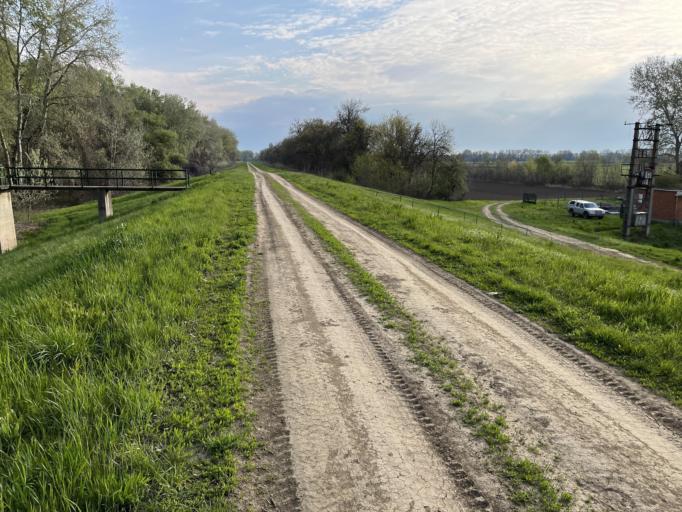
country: HU
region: Jasz-Nagykun-Szolnok
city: Szajol
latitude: 47.1861
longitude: 20.2883
